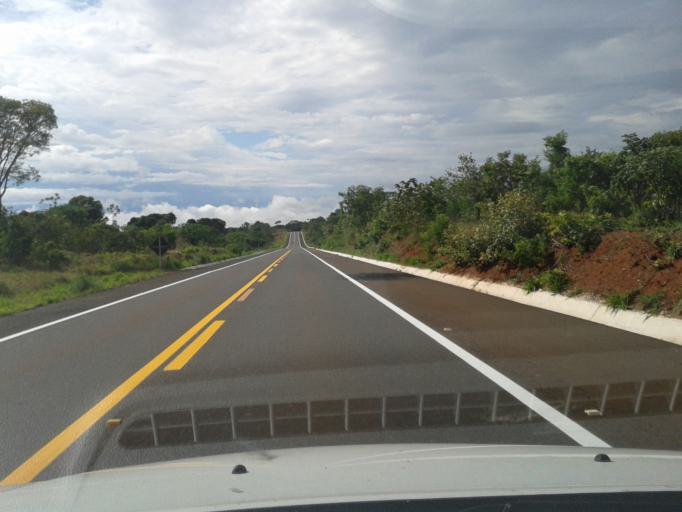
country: BR
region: Minas Gerais
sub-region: Campina Verde
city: Campina Verde
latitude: -19.3155
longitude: -49.6618
